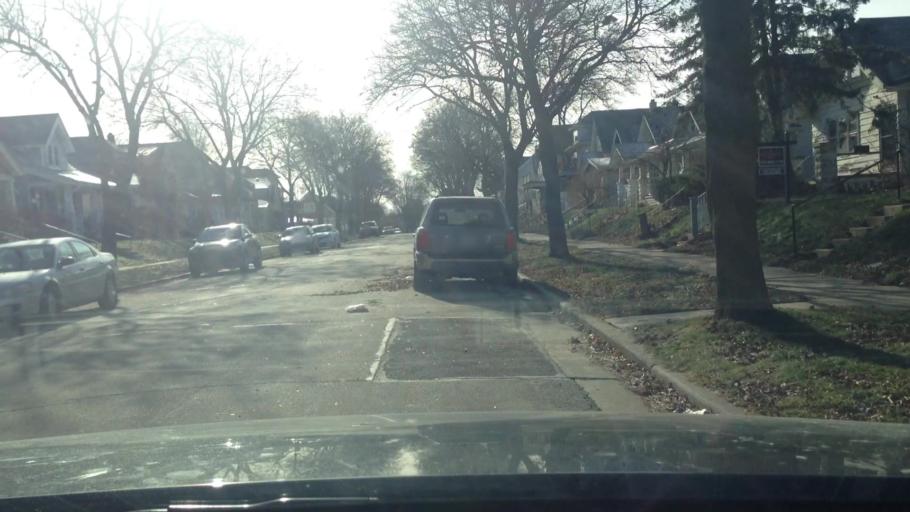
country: US
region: Wisconsin
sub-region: Milwaukee County
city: Shorewood
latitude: 43.0814
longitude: -87.9001
